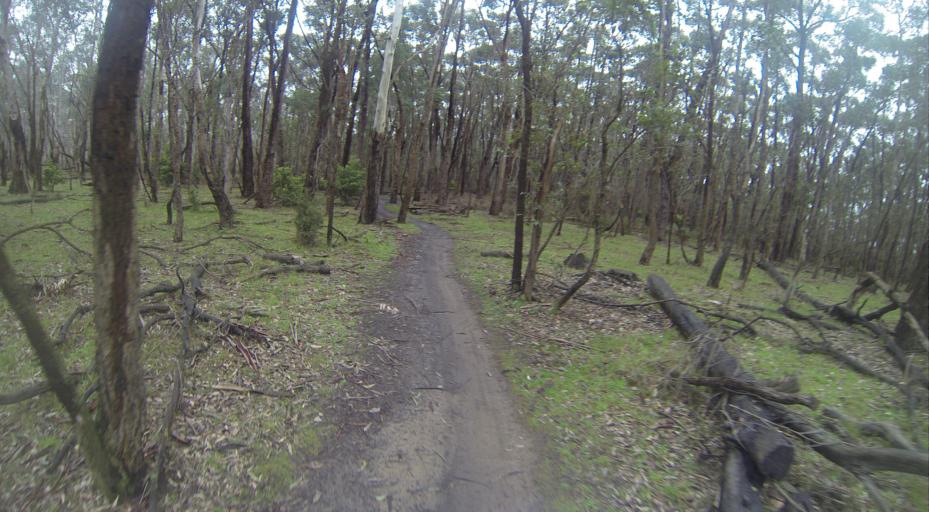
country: AU
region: Victoria
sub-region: Yarra Ranges
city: Lysterfield
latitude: -37.9591
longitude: 145.3018
